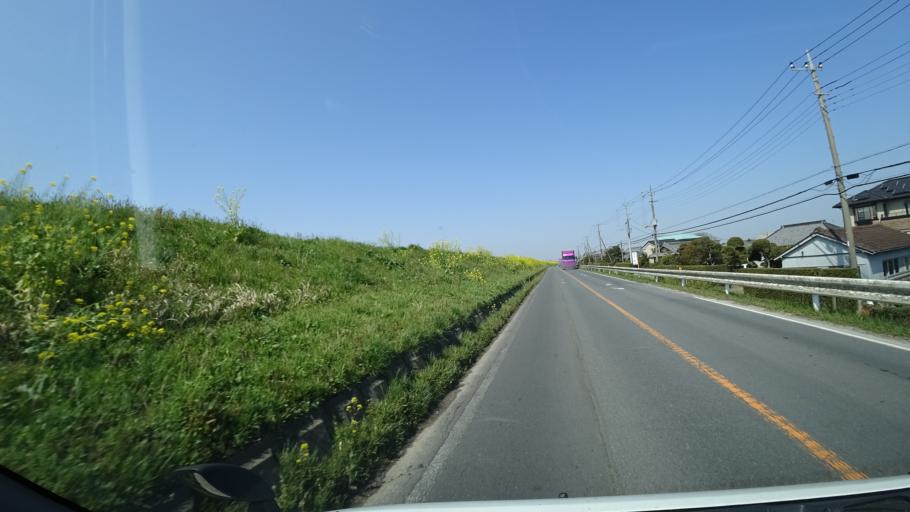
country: JP
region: Chiba
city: Katori-shi
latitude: 35.9106
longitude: 140.4127
